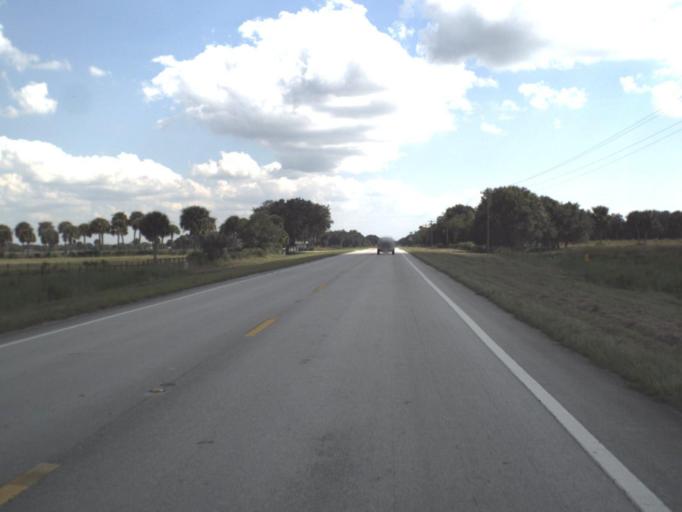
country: US
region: Florida
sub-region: Okeechobee County
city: Okeechobee
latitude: 27.3302
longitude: -80.9279
